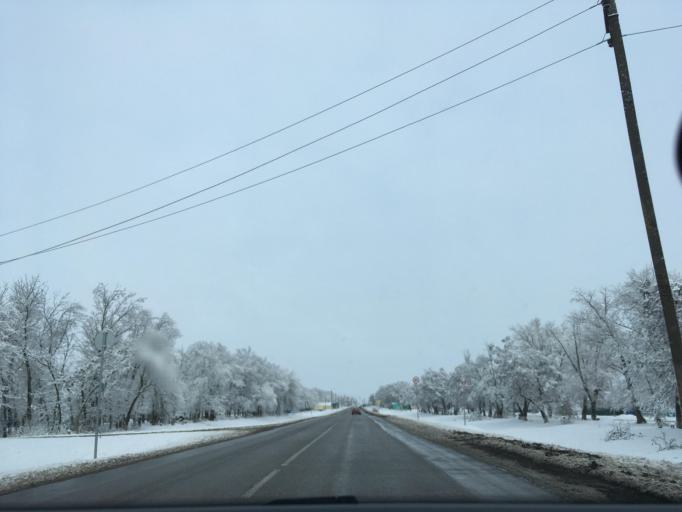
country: RU
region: Voronezj
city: Ol'khovatka
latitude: 50.0357
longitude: 39.0745
